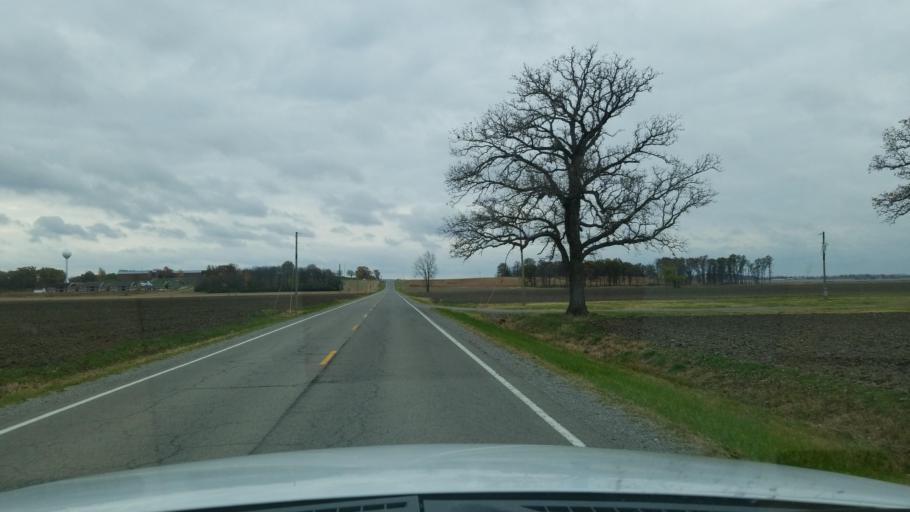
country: US
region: Illinois
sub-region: Saline County
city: Eldorado
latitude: 37.7610
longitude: -88.4383
